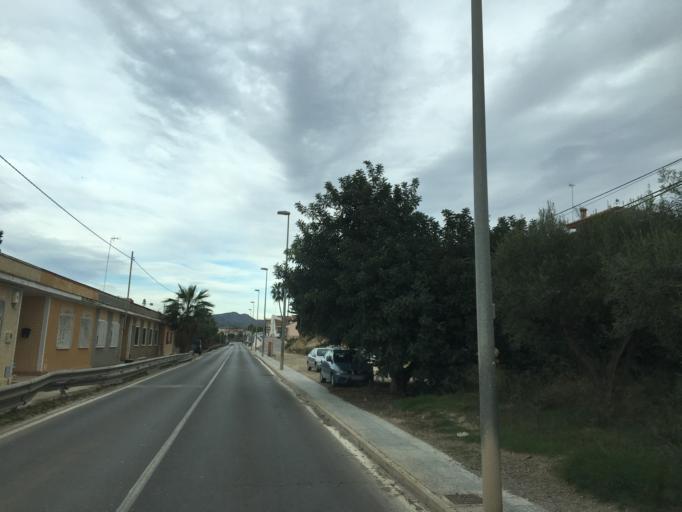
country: ES
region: Murcia
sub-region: Murcia
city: Cartagena
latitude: 37.6115
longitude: -1.0317
